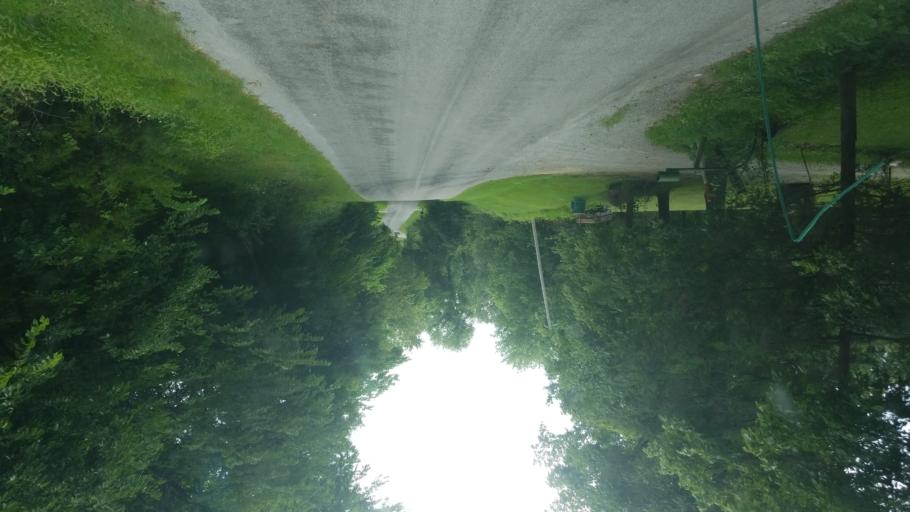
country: US
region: Illinois
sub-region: Jackson County
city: Murphysboro
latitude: 37.6812
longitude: -89.3878
